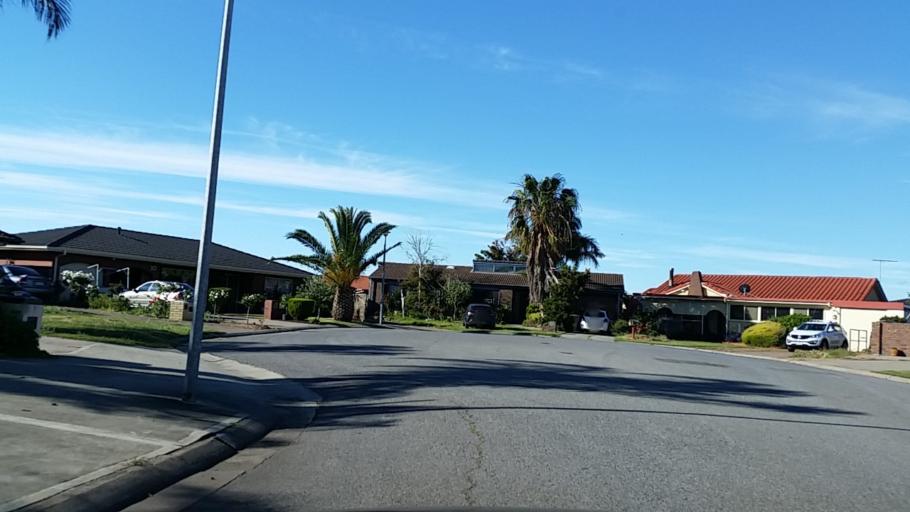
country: AU
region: South Australia
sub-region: Charles Sturt
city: West Lakes Shore
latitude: -34.8691
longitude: 138.4951
